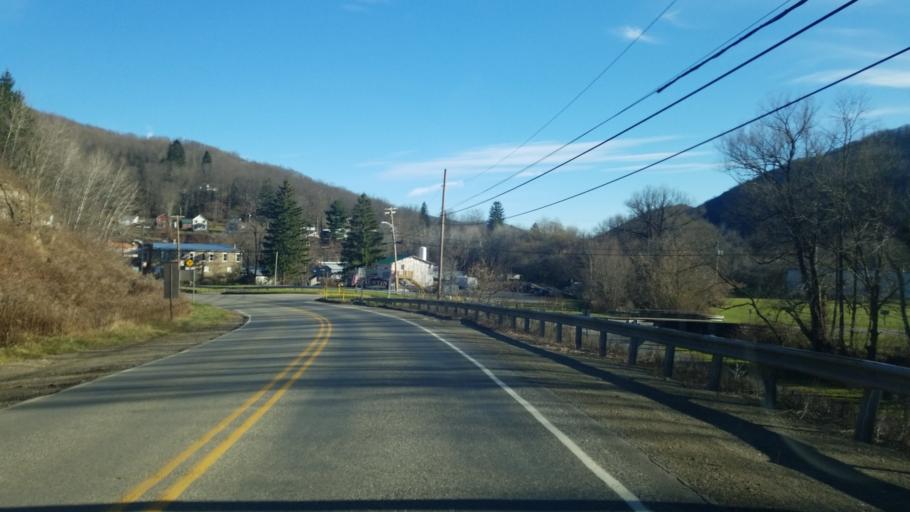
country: US
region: Pennsylvania
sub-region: Potter County
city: Coudersport
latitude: 41.6314
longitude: -78.0945
